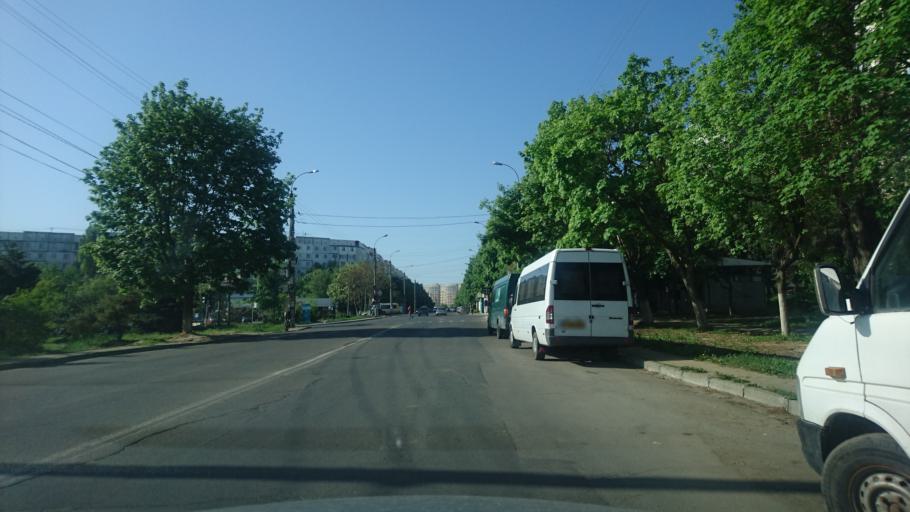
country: MD
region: Chisinau
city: Vatra
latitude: 47.0438
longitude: 28.7703
